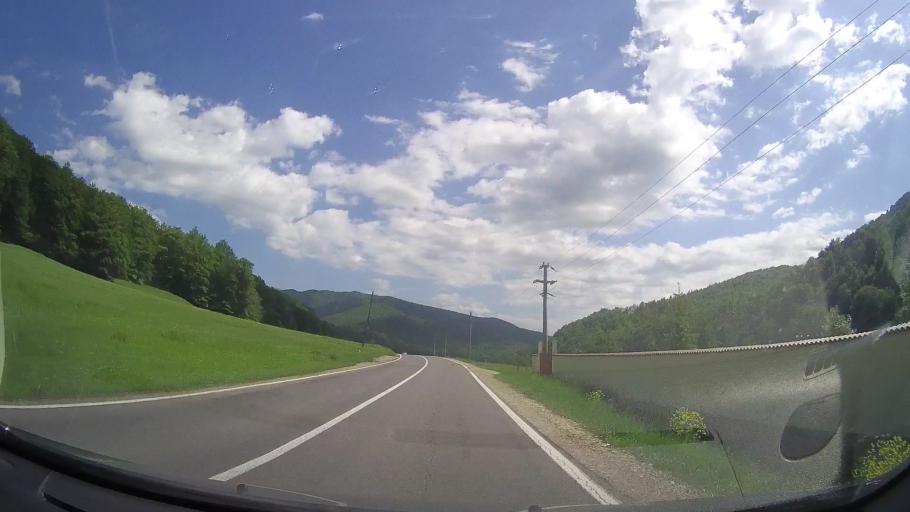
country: RO
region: Prahova
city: Maneciu
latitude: 45.4299
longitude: 25.9391
